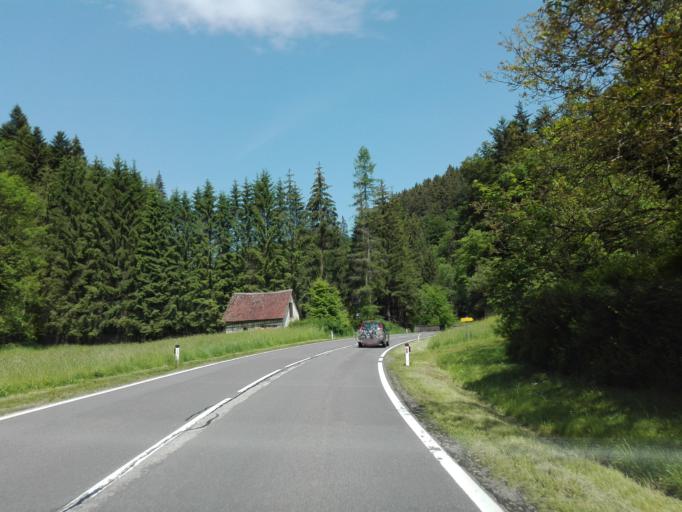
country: AT
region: Upper Austria
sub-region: Politischer Bezirk Rohrbach
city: Atzesberg
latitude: 48.4125
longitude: 13.8818
